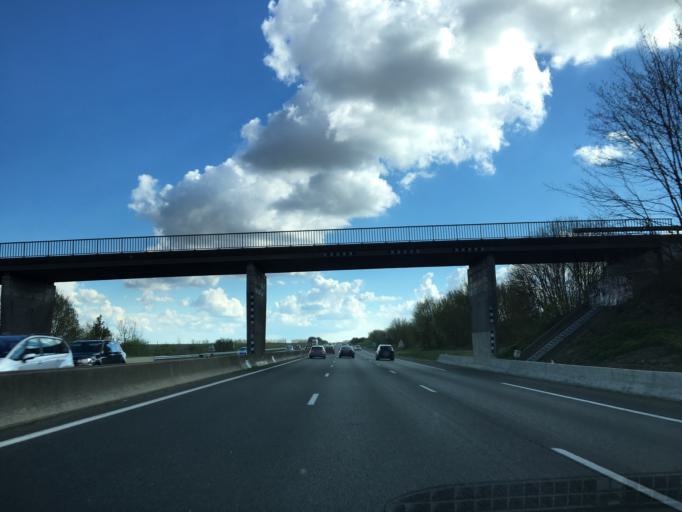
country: FR
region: Nord-Pas-de-Calais
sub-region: Departement du Pas-de-Calais
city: Vaulx-Vraucourt
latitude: 50.1487
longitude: 2.8726
